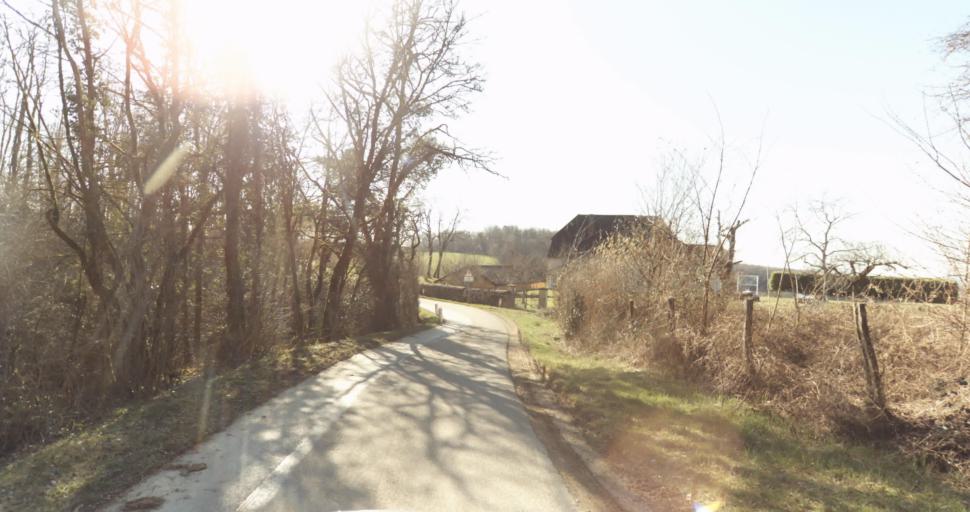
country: FR
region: Franche-Comte
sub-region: Departement du Jura
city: Montmorot
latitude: 46.7008
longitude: 5.5203
